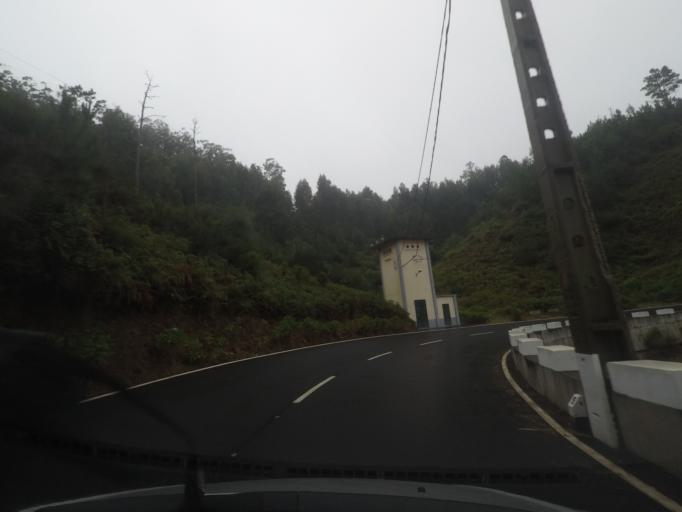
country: PT
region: Madeira
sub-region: Santa Cruz
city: Camacha
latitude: 32.6969
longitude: -16.8392
